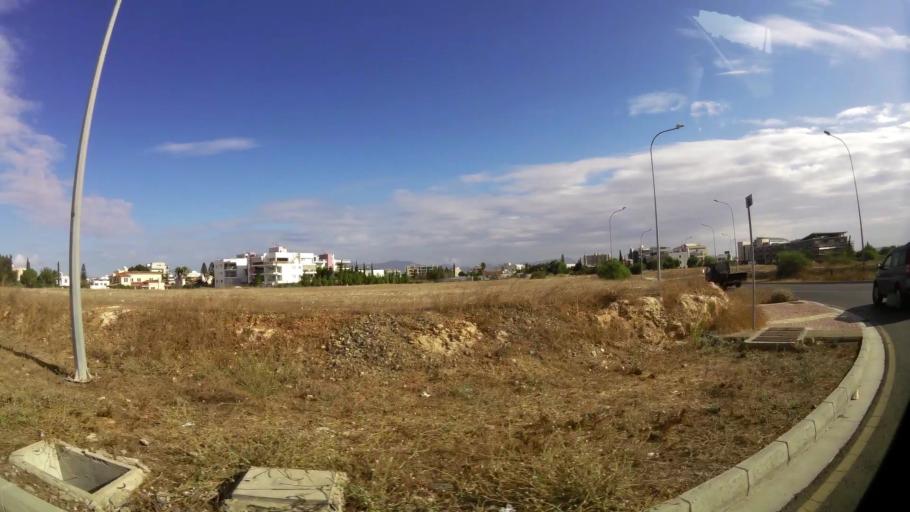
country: CY
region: Lefkosia
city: Nicosia
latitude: 35.1368
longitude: 33.3689
